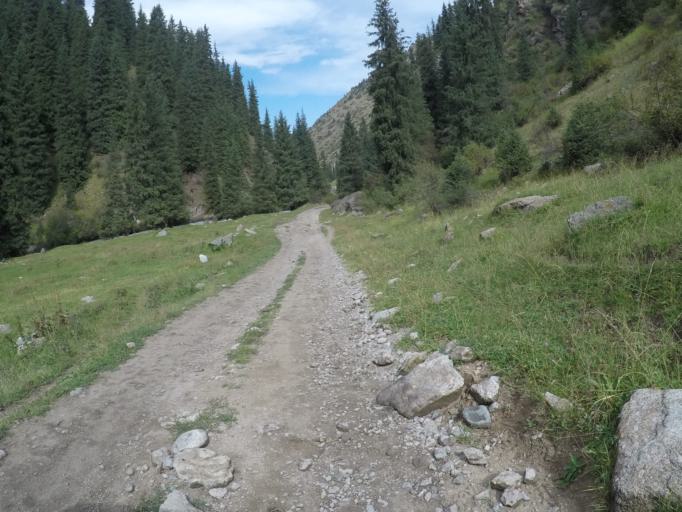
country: KG
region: Ysyk-Koel
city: Teploklyuchenka
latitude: 42.4372
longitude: 78.5606
